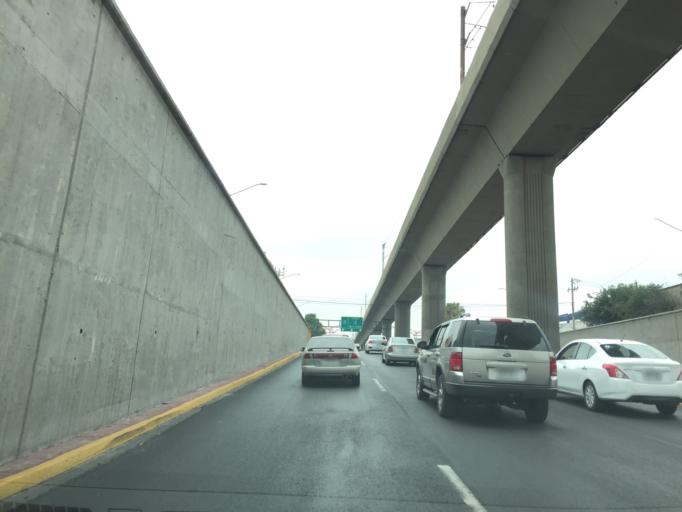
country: MX
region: Nuevo Leon
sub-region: Monterrey
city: Monterrey
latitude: 25.6837
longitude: -100.2924
